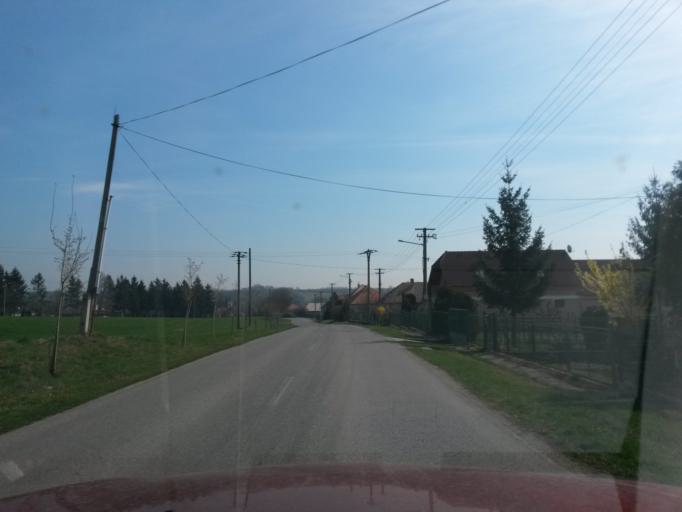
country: SK
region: Nitriansky
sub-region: Okres Nitra
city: Vrable
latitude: 48.1095
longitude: 18.4149
